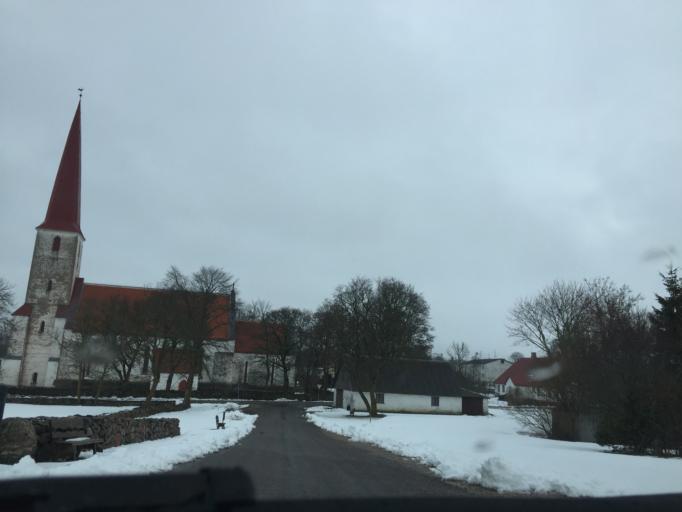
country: EE
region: Saare
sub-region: Kuressaare linn
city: Kuressaare
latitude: 58.3591
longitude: 22.0358
